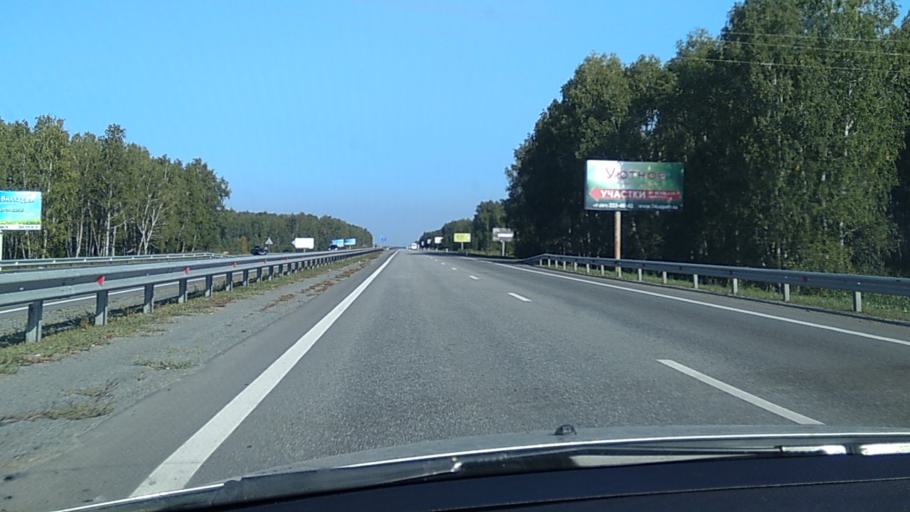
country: RU
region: Chelyabinsk
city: Sargazy
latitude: 55.0084
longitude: 61.2161
